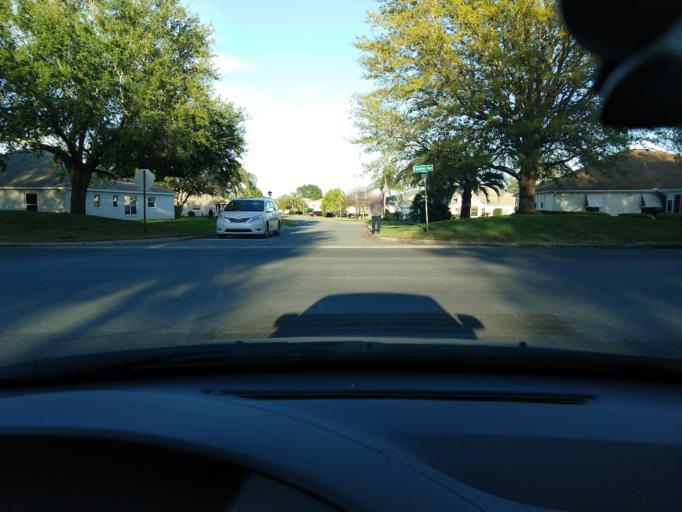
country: US
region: Florida
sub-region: Sumter County
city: The Villages
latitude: 28.9495
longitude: -81.9759
